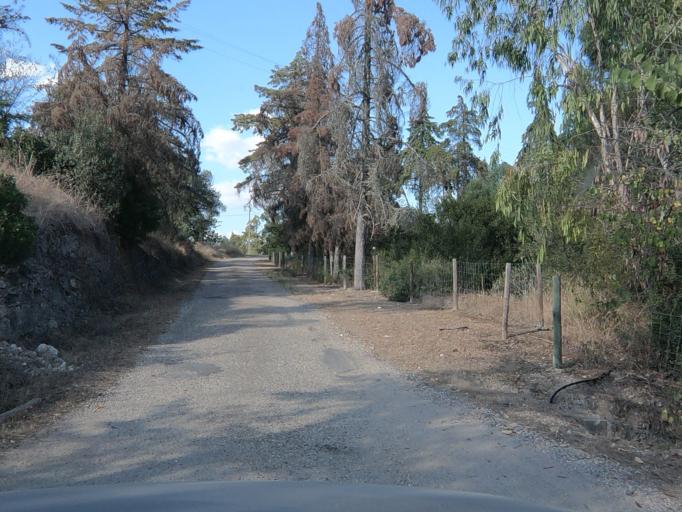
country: PT
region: Setubal
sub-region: Alcacer do Sal
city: Alcacer do Sal
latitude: 38.2495
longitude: -8.2955
